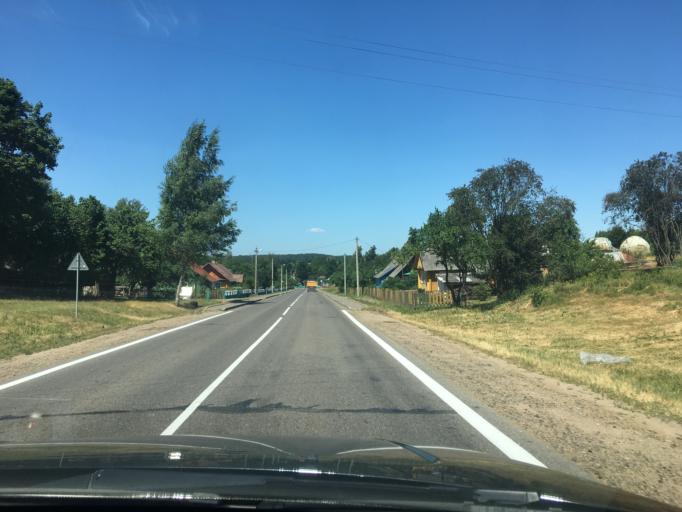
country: BY
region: Grodnenskaya
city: Hal'shany
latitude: 54.1522
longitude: 25.9112
